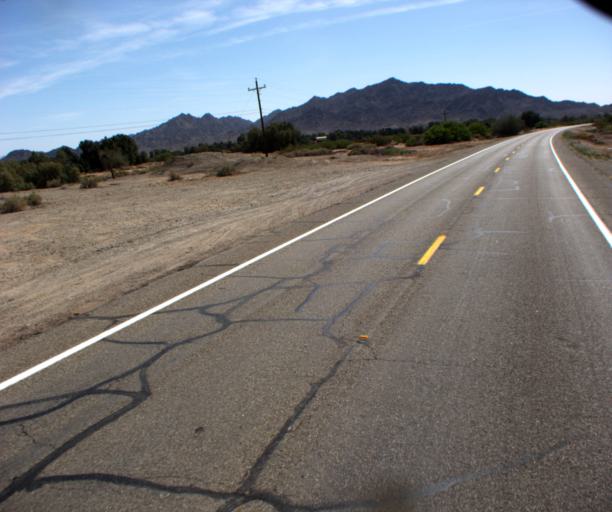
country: US
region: Arizona
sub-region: Yuma County
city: Fortuna Foothills
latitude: 32.7816
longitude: -114.3824
